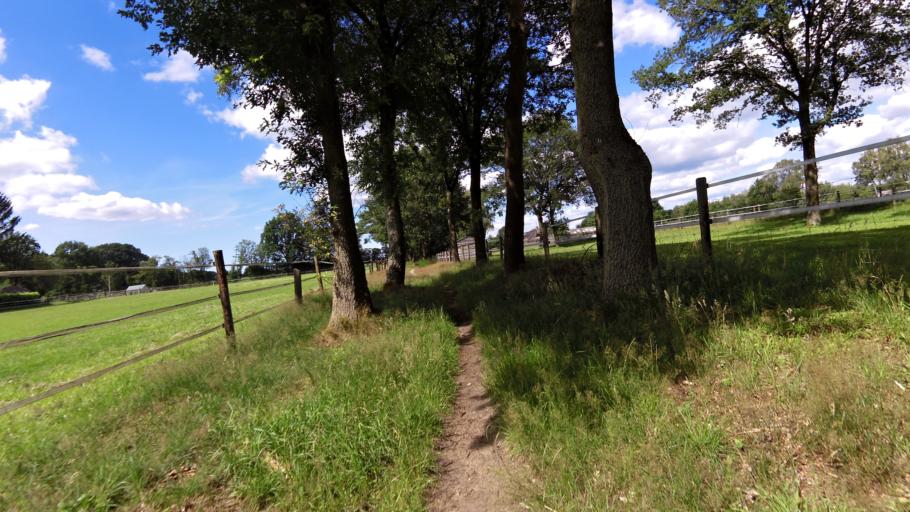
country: NL
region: Gelderland
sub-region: Gemeente Epe
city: Vaassen
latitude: 52.2668
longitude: 5.9419
